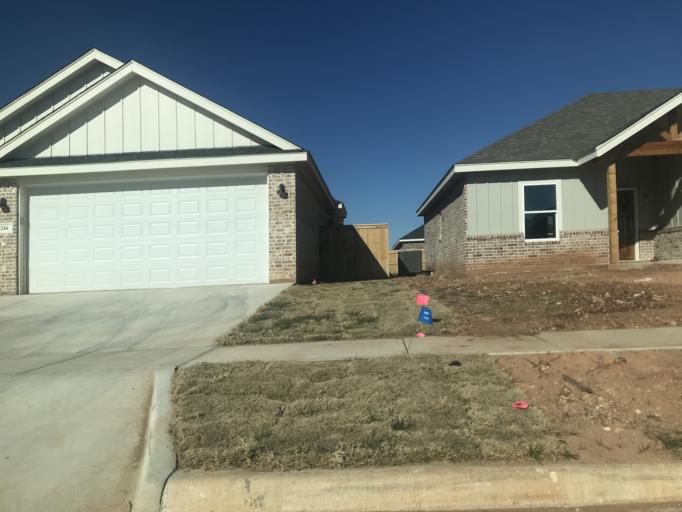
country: US
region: Texas
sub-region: Taylor County
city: Potosi
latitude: 32.3695
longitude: -99.7202
